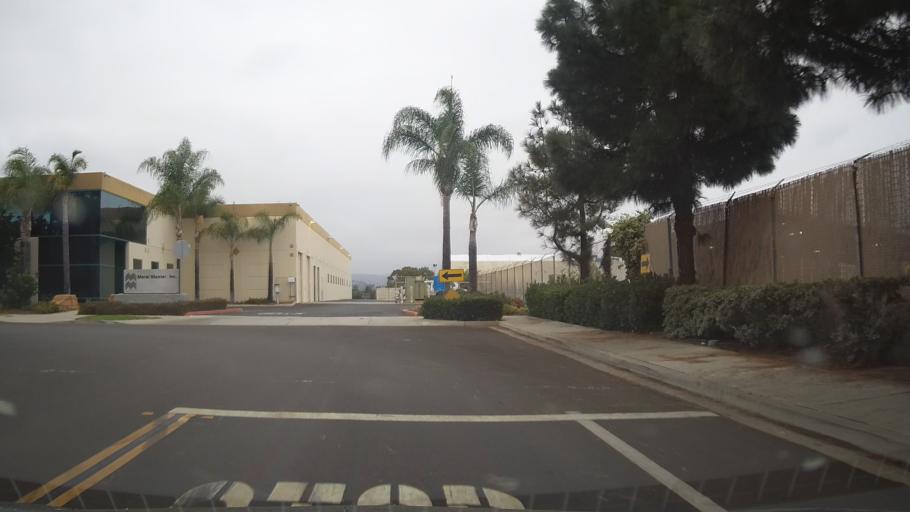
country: US
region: California
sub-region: San Diego County
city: San Diego
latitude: 32.8249
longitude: -117.1330
